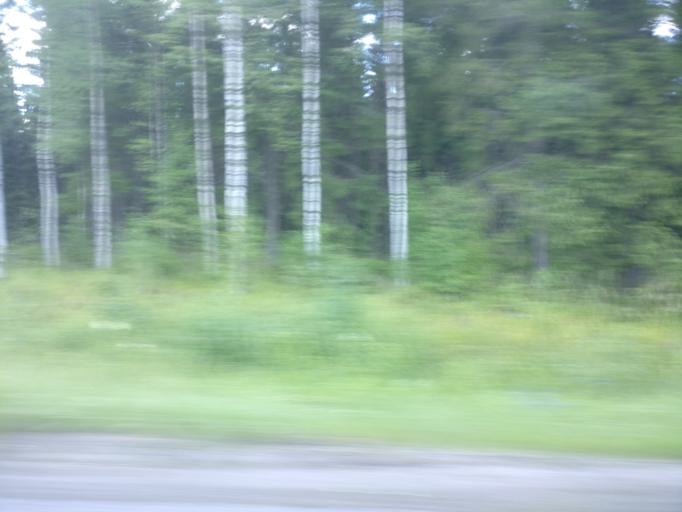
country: FI
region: Uusimaa
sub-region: Helsinki
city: Hyvinge
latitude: 60.5887
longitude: 24.8430
